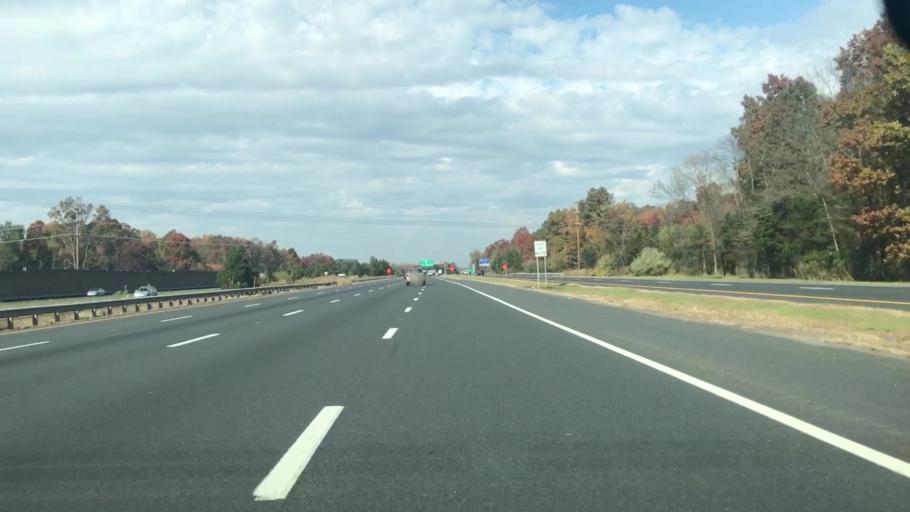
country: US
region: New Jersey
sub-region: Somerset County
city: Bridgewater
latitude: 40.6172
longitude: -74.6346
